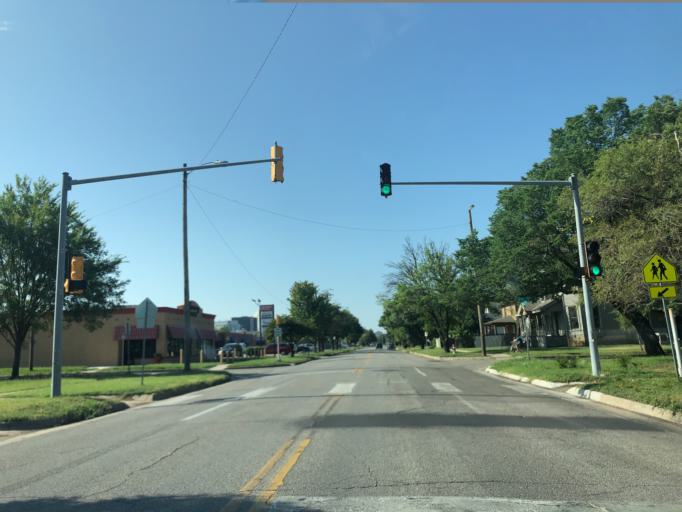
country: US
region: Kansas
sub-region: Sedgwick County
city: Wichita
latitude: 37.7031
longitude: -97.3420
